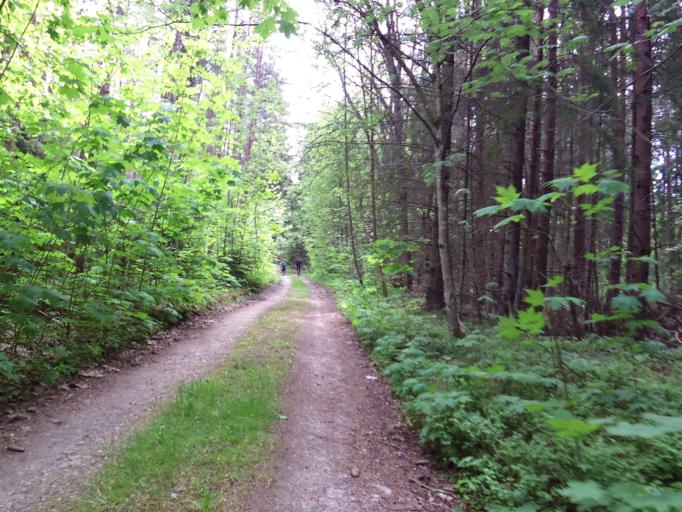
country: EE
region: Harju
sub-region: Paldiski linn
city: Paldiski
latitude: 59.2530
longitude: 23.7491
